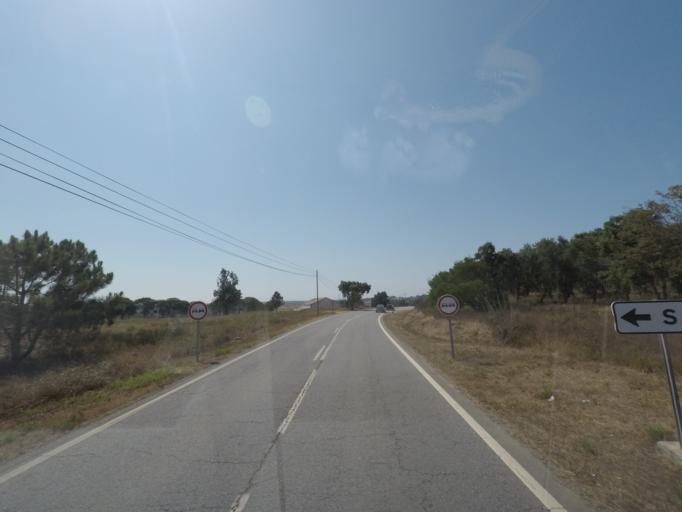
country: PT
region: Beja
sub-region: Odemira
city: Sao Teotonio
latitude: 37.5228
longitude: -8.7009
